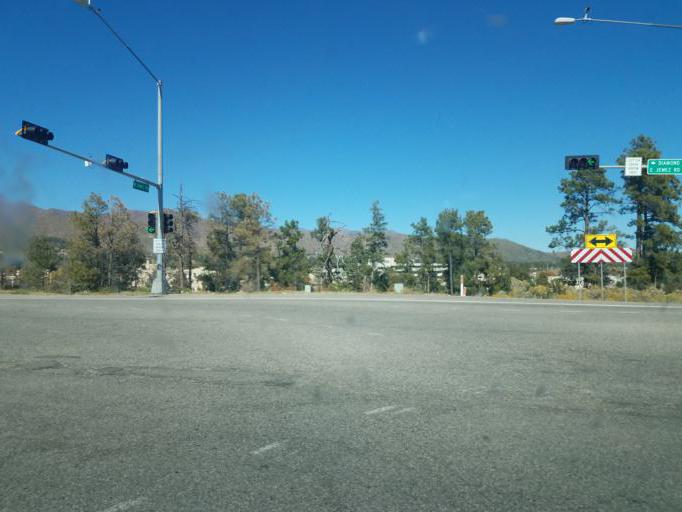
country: US
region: New Mexico
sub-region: Los Alamos County
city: Los Alamos
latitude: 35.8784
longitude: -106.3188
